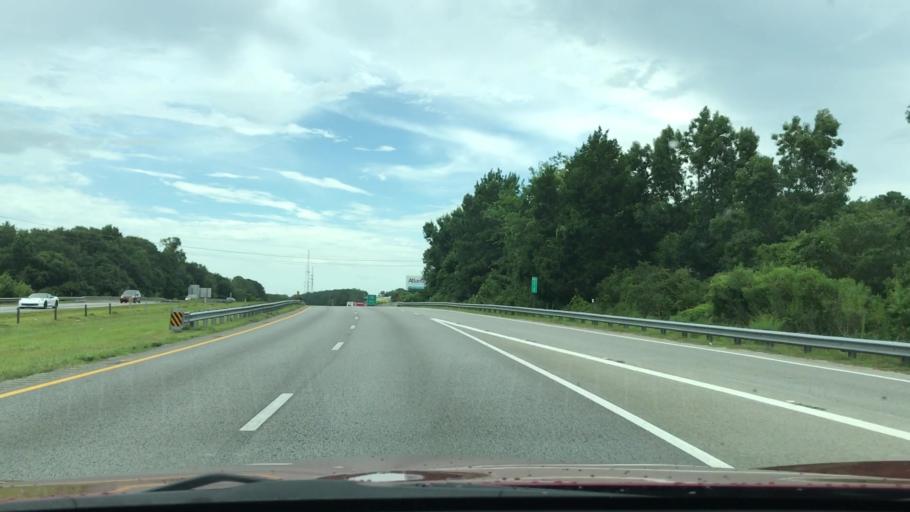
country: US
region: South Carolina
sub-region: Charleston County
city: Shell Point
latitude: 32.8067
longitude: -80.0371
